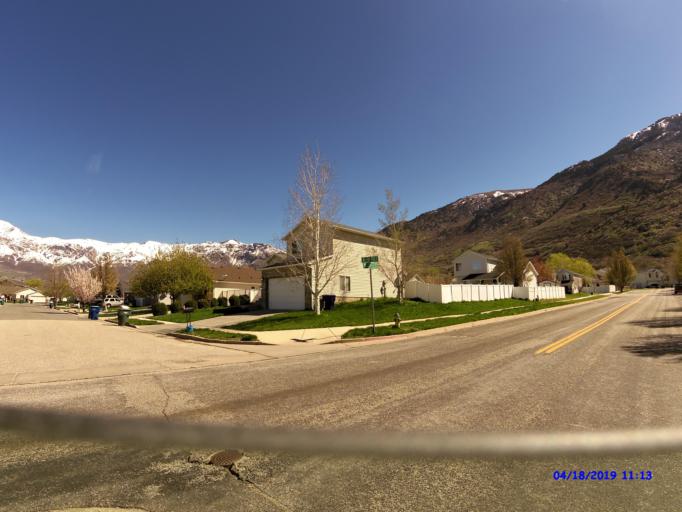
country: US
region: Utah
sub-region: Weber County
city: North Ogden
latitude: 41.2825
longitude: -111.9535
